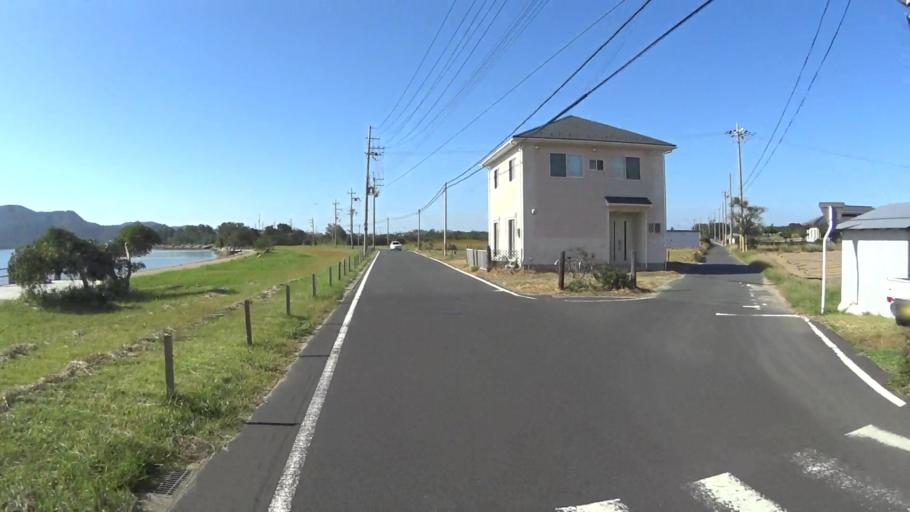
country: JP
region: Hyogo
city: Toyooka
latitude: 35.6407
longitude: 134.9227
